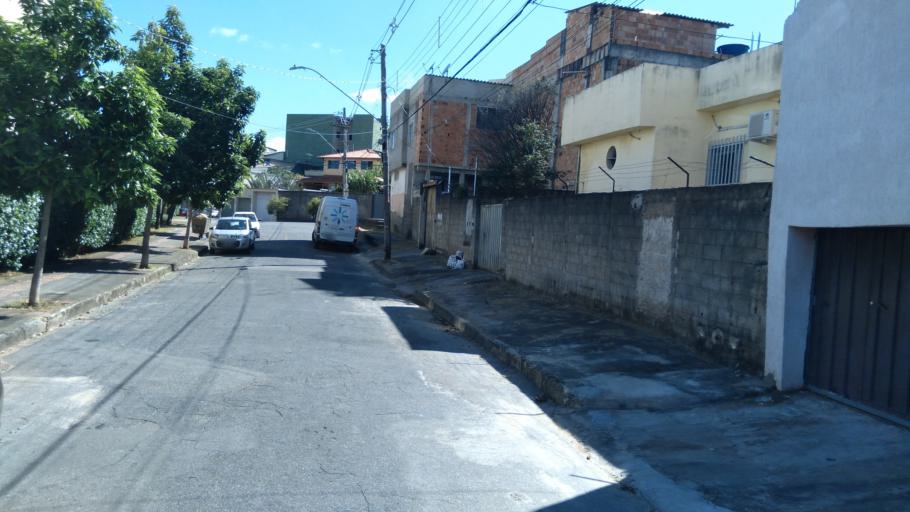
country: BR
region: Minas Gerais
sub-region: Belo Horizonte
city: Belo Horizonte
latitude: -19.8561
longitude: -43.9122
